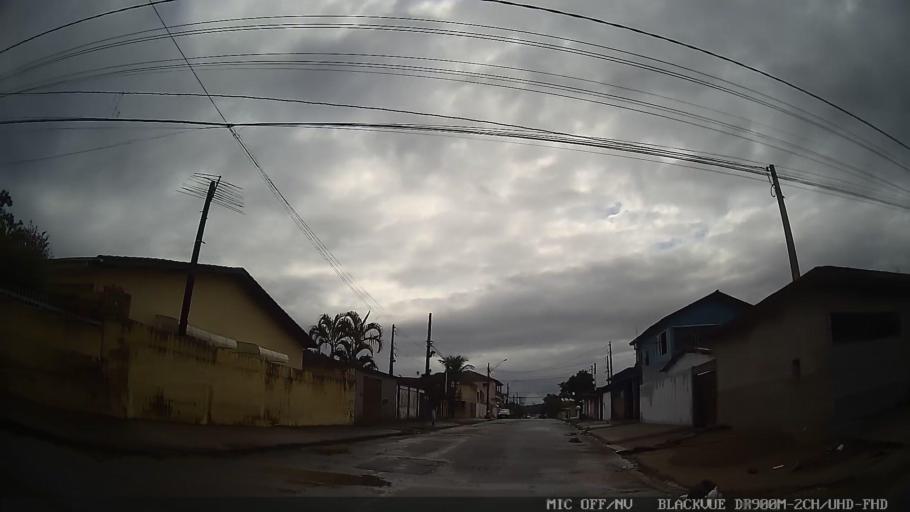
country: BR
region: Sao Paulo
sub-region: Itanhaem
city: Itanhaem
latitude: -24.1902
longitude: -46.8139
